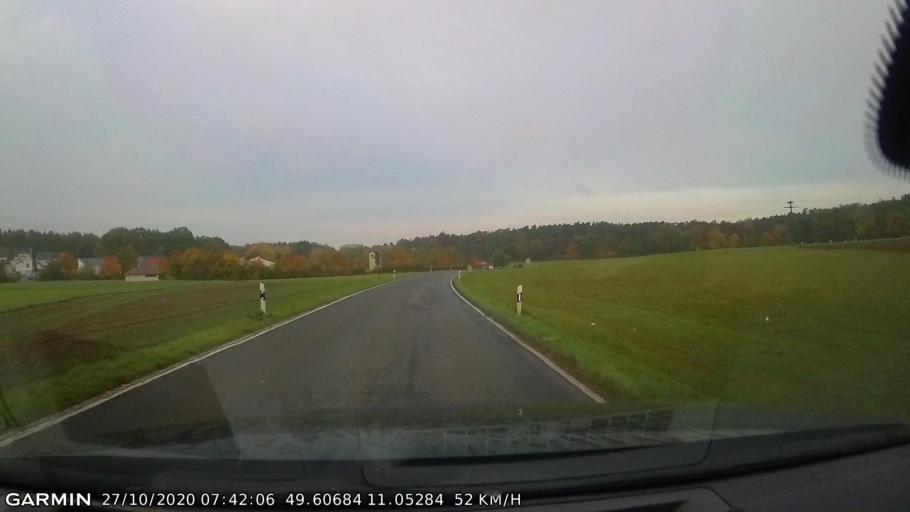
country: DE
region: Bavaria
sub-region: Regierungsbezirk Mittelfranken
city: Spardorf
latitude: 49.6073
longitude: 11.0522
